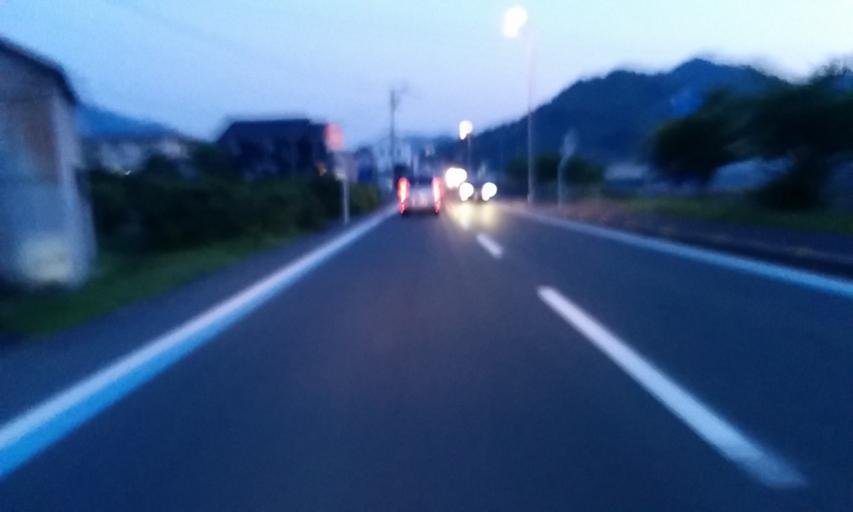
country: JP
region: Ehime
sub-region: Nishiuwa-gun
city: Ikata-cho
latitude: 33.4967
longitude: 132.3972
